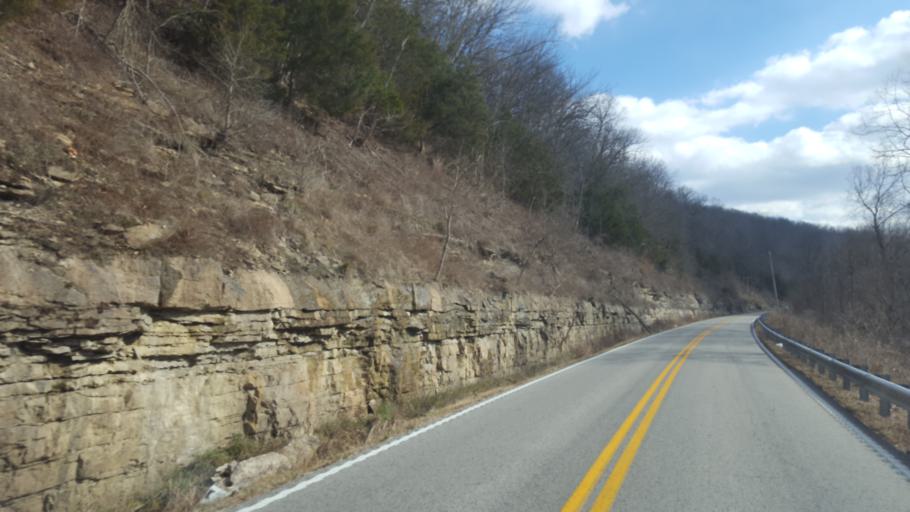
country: US
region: Kentucky
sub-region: Owen County
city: Owenton
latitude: 38.4617
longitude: -84.9135
